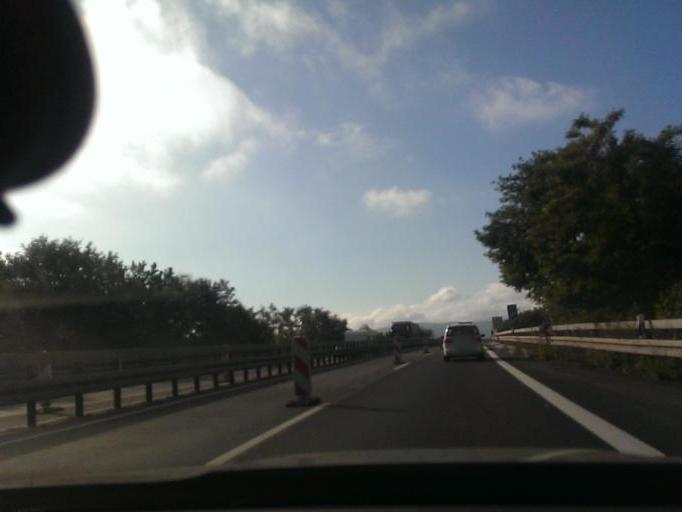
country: DE
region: Lower Saxony
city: Vienenburg
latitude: 51.9510
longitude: 10.5838
